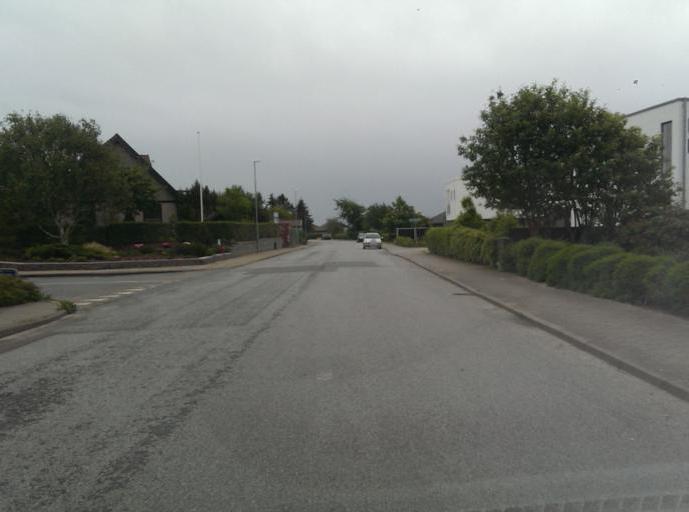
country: DK
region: South Denmark
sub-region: Fano Kommune
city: Nordby
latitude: 55.5292
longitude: 8.3500
